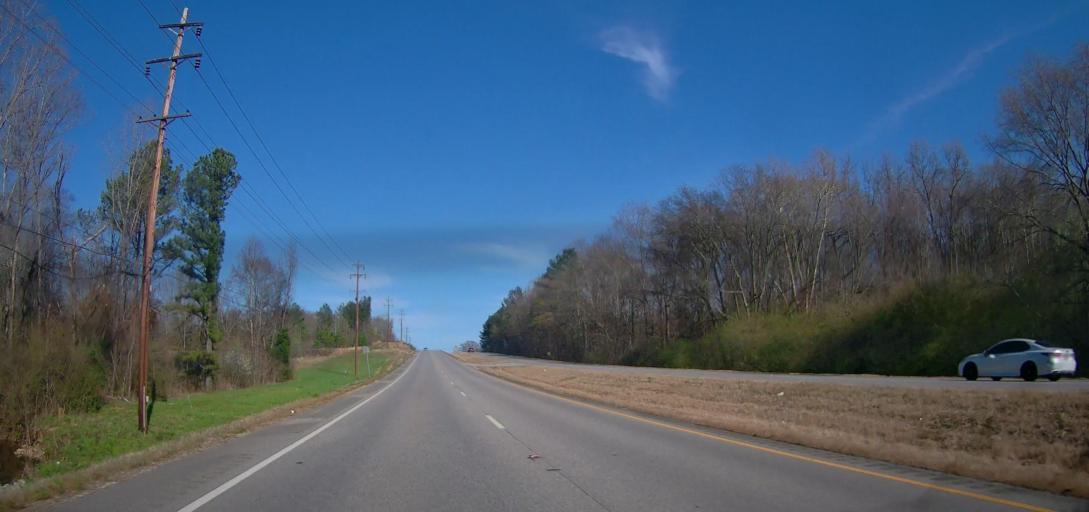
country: US
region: Alabama
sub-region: Lauderdale County
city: Killen
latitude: 34.8597
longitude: -87.4845
